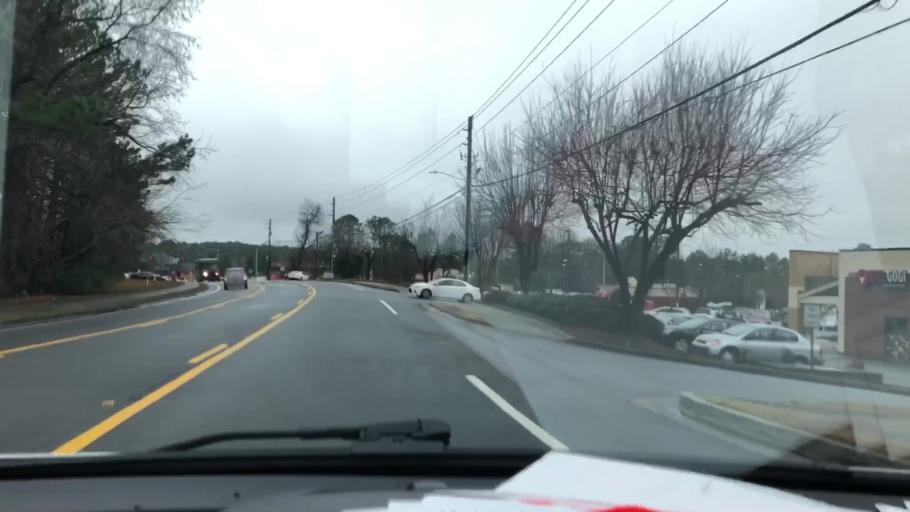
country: US
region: Georgia
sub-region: Gwinnett County
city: Norcross
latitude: 33.9693
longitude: -84.2188
